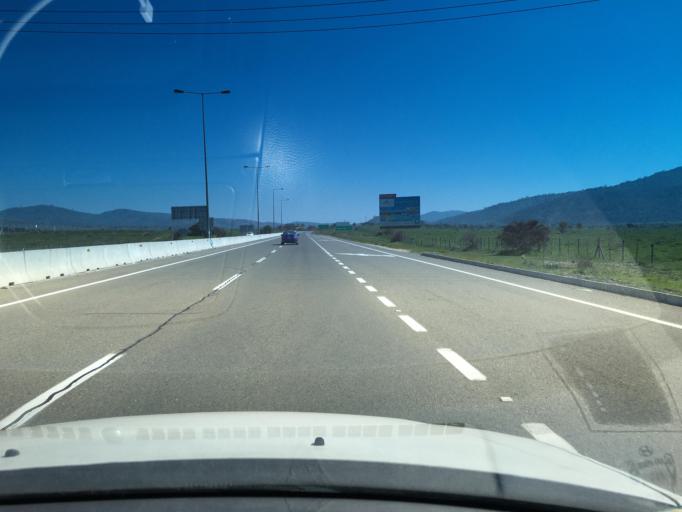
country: CL
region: Valparaiso
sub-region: San Antonio Province
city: Cartagena
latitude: -33.3900
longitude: -71.4393
